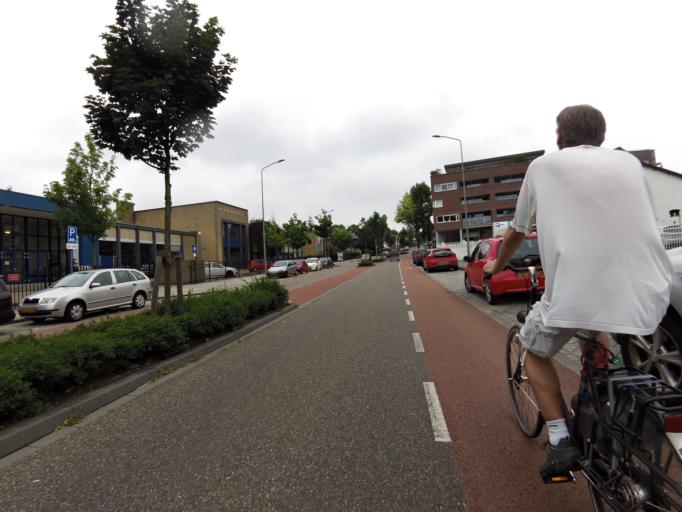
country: NL
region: Limburg
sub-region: Gemeente Heerlen
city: Heerlen
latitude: 50.8797
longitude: 5.9859
